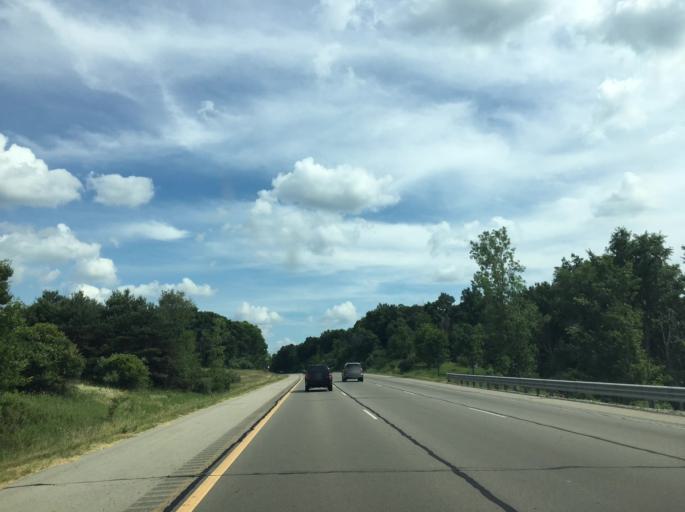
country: US
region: Michigan
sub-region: Oakland County
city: Clarkston
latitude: 42.7534
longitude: -83.5028
